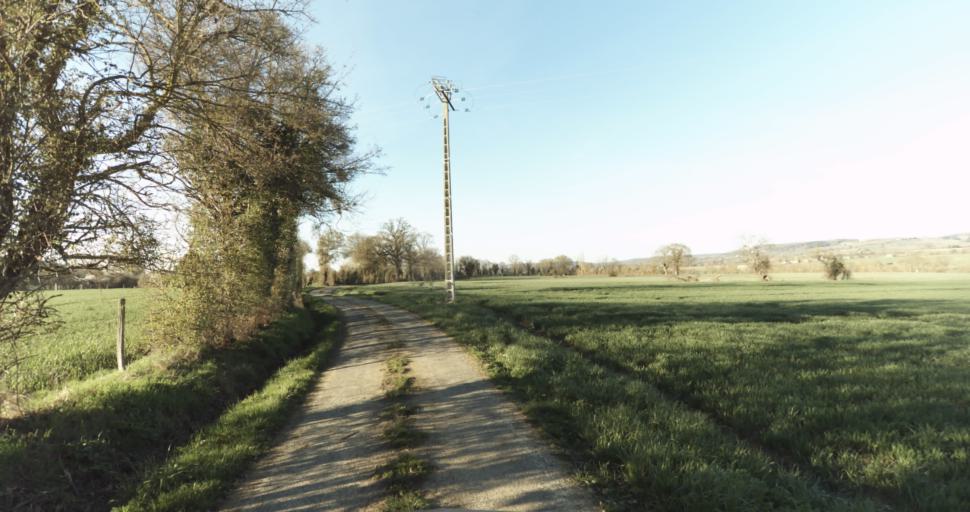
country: FR
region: Lower Normandy
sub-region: Departement de l'Orne
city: Trun
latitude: 48.9075
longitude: 0.0174
